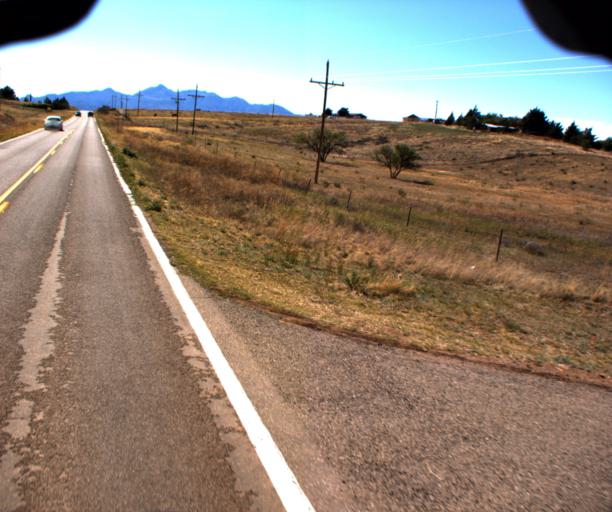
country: US
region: Arizona
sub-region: Cochise County
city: Huachuca City
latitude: 31.6736
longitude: -110.6246
